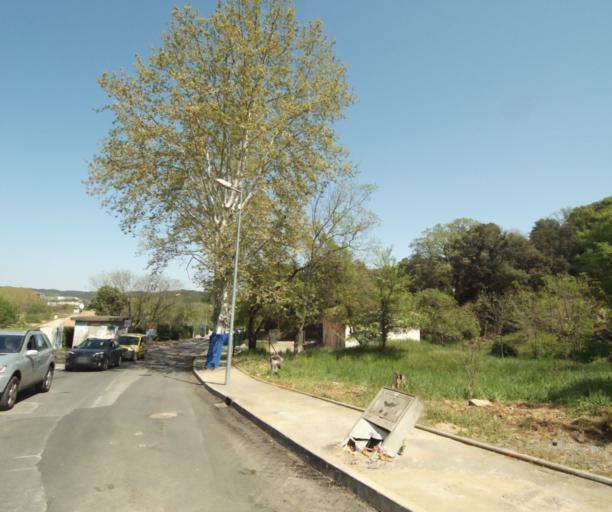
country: FR
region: Languedoc-Roussillon
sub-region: Departement de l'Herault
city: Montferrier-sur-Lez
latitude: 43.6686
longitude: 3.8598
